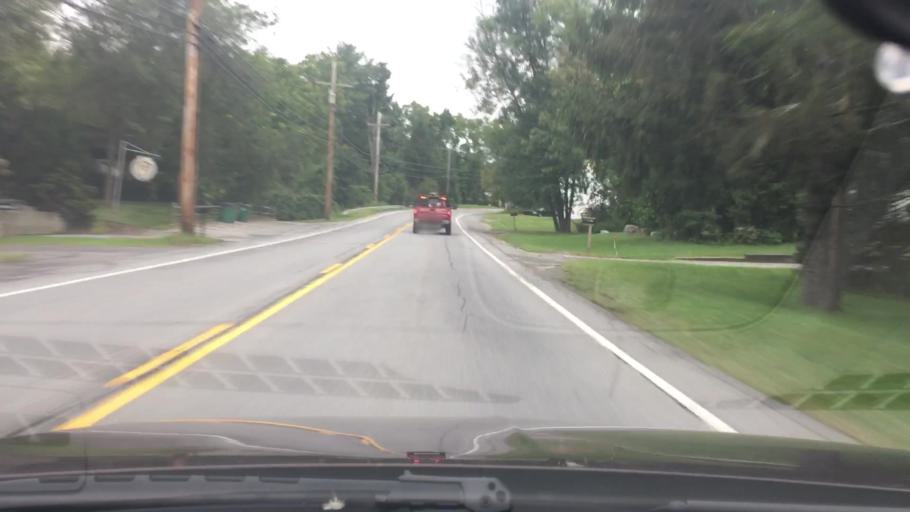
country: US
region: New York
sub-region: Dutchess County
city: Pleasant Valley
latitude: 41.7564
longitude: -73.7881
